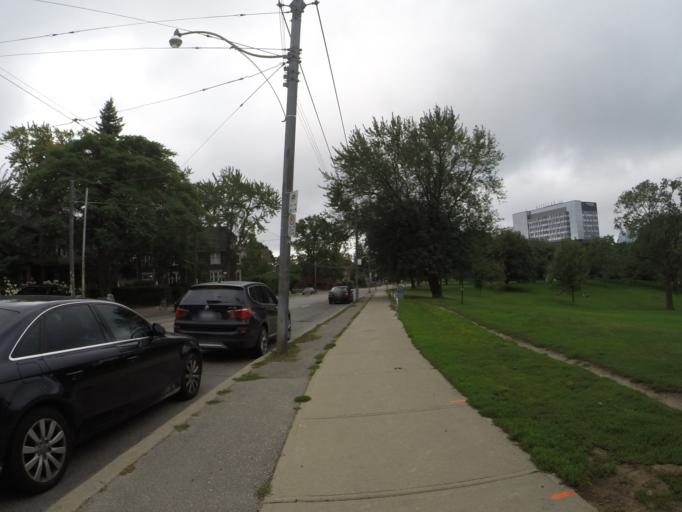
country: CA
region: Ontario
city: Toronto
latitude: 43.6704
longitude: -79.3539
